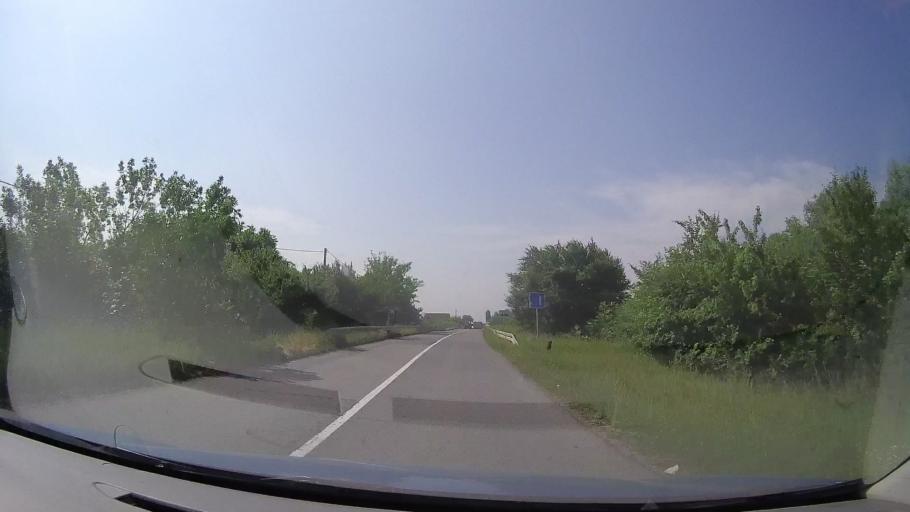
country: RS
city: Jarkovac
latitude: 45.2741
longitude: 20.7645
